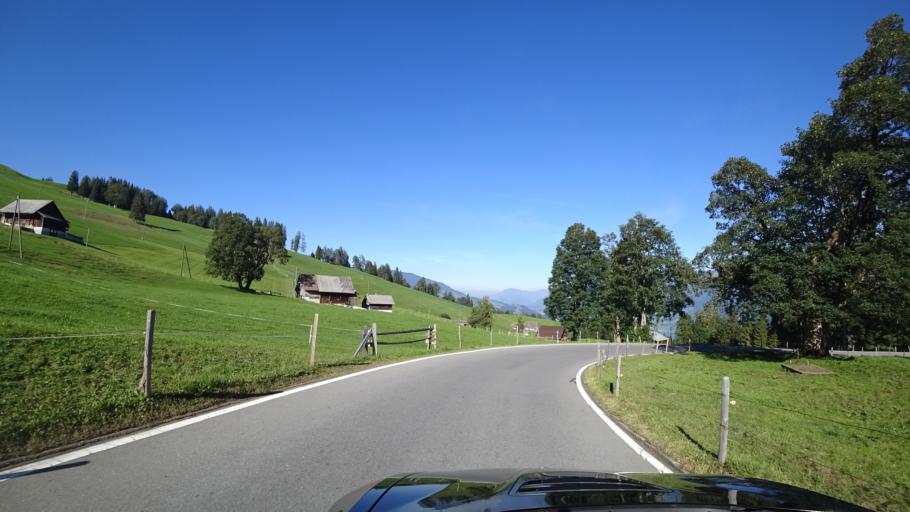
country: CH
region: Obwalden
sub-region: Obwalden
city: Giswil
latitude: 46.8332
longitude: 8.1281
